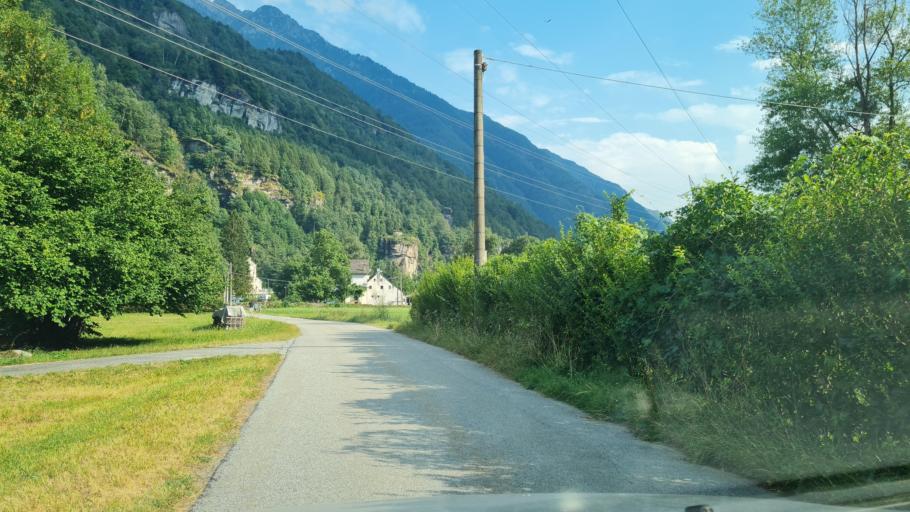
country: IT
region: Piedmont
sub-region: Provincia Verbano-Cusio-Ossola
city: Baceno
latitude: 46.2493
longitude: 8.3289
